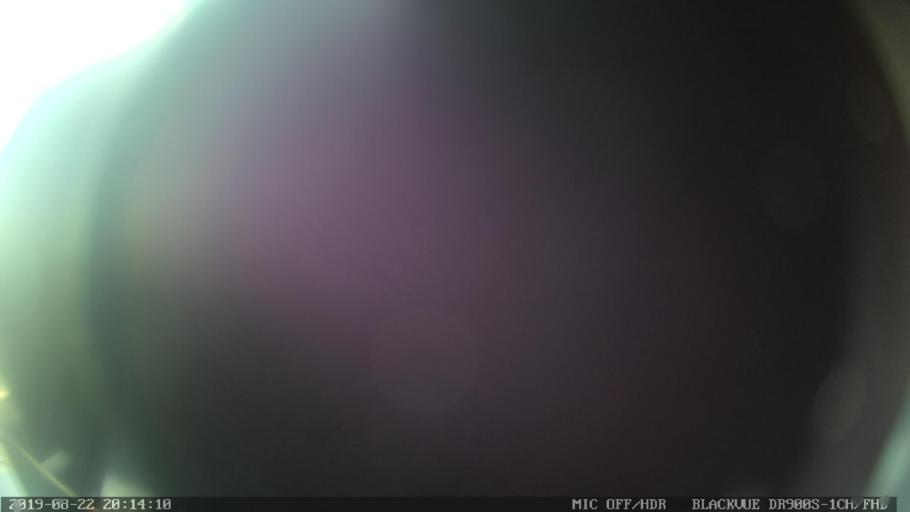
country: PT
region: Guarda
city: Alcains
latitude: 39.9231
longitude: -7.4218
